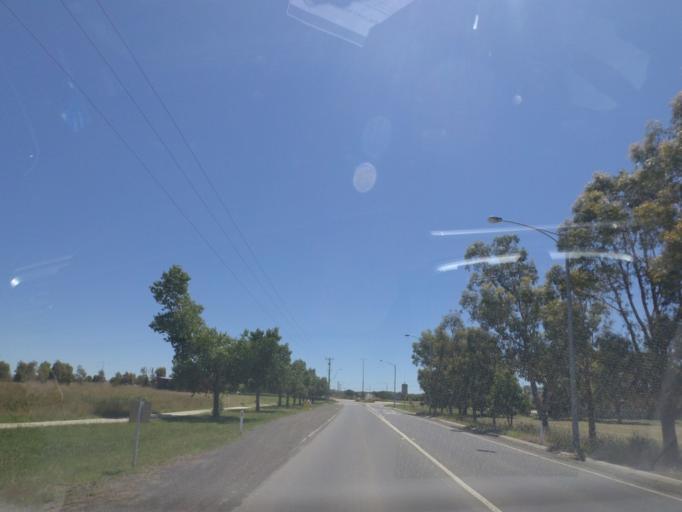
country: AU
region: Victoria
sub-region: Whittlesea
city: Whittlesea
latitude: -37.4192
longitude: 145.0040
